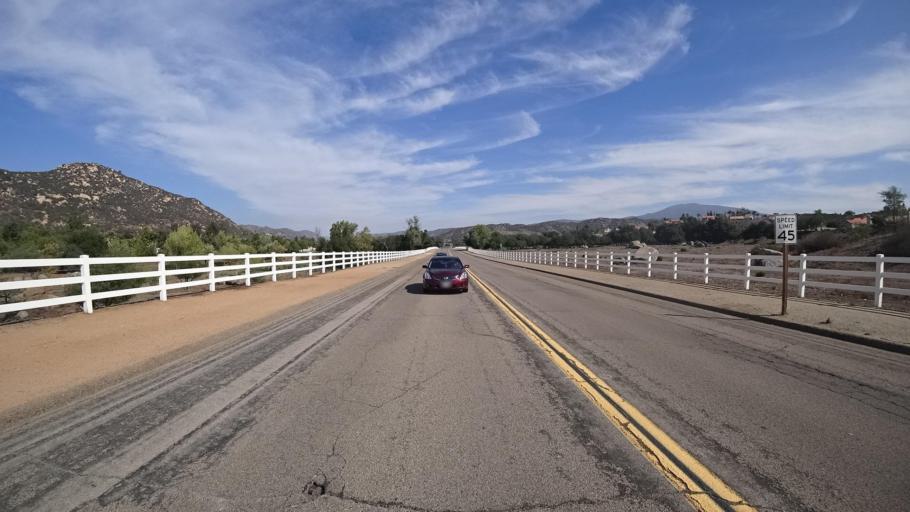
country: US
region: California
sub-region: San Diego County
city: Harbison Canyon
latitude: 32.8366
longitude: -116.8120
